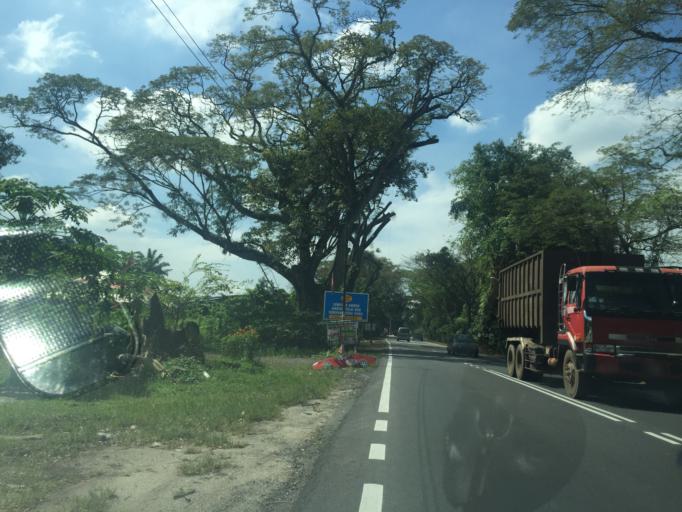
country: MY
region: Penang
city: Tasek Glugor
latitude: 5.5066
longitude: 100.5280
